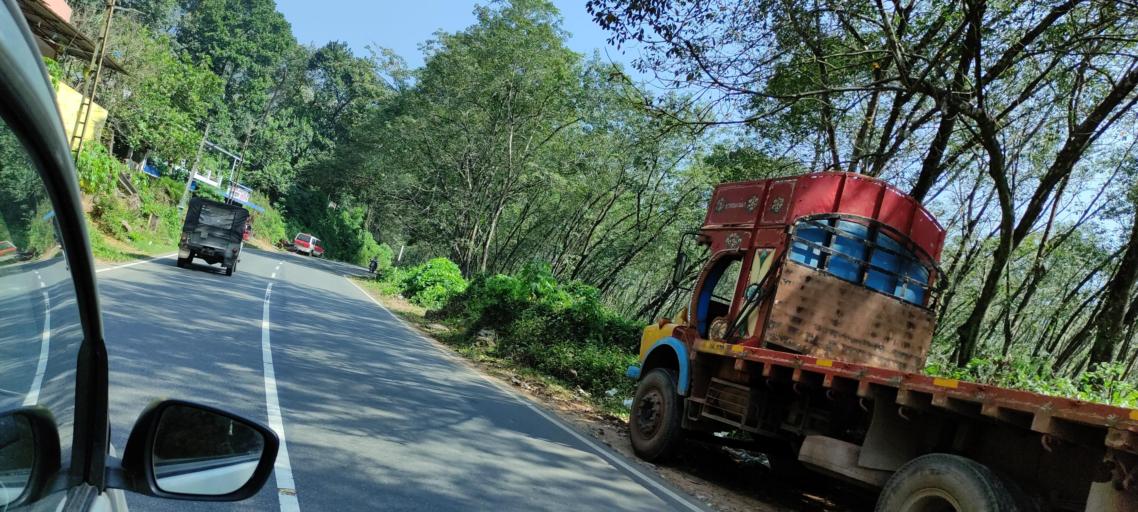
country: IN
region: Kerala
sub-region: Kollam
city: Punalur
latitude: 8.9740
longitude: 77.0602
